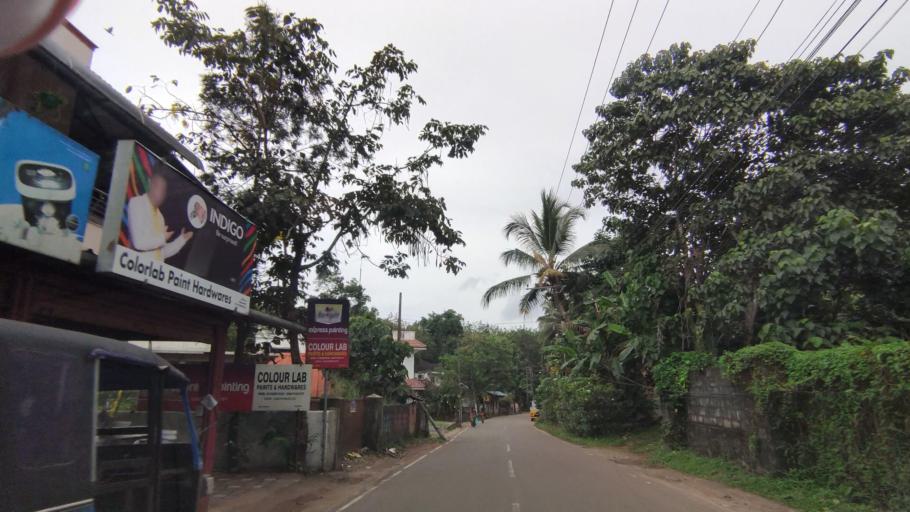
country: IN
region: Kerala
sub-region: Kottayam
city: Kottayam
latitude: 9.6543
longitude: 76.5250
